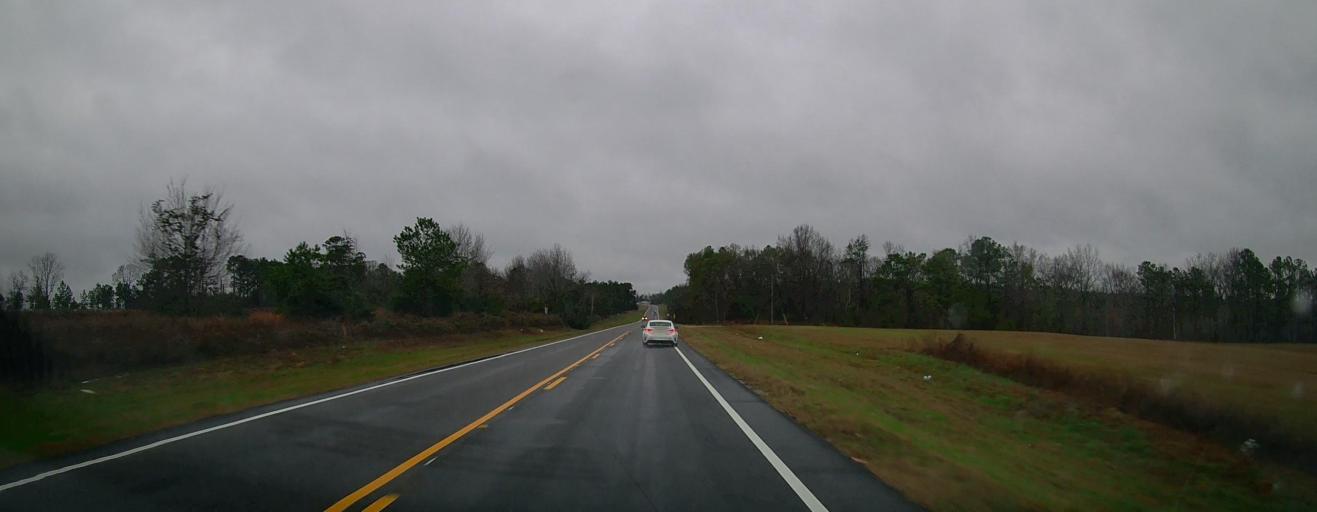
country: US
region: Alabama
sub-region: Chilton County
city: Clanton
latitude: 32.6772
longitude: -86.7901
